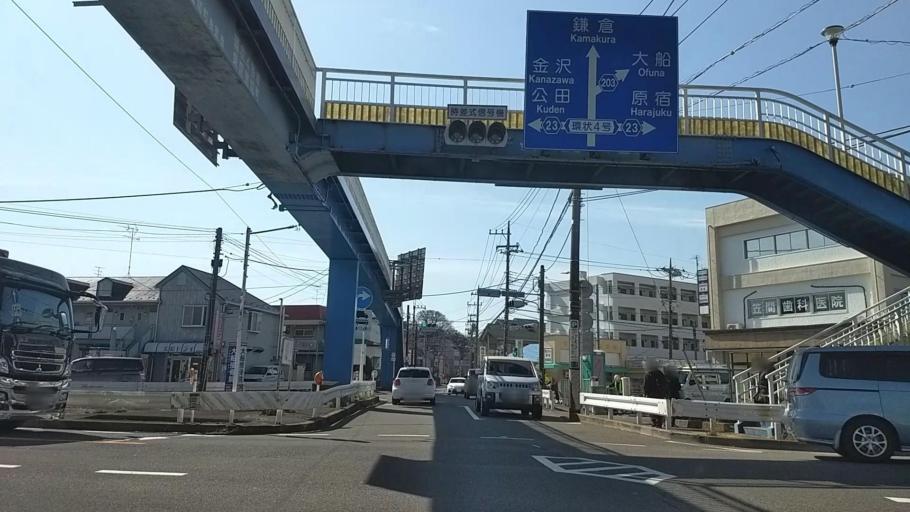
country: JP
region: Kanagawa
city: Kamakura
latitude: 35.3619
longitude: 139.5408
